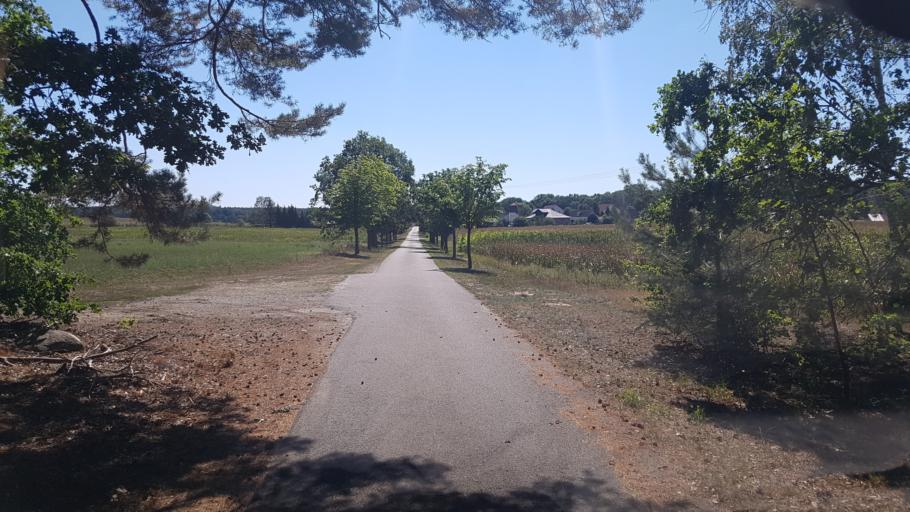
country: DE
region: Brandenburg
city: Altdobern
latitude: 51.6951
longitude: 14.0021
